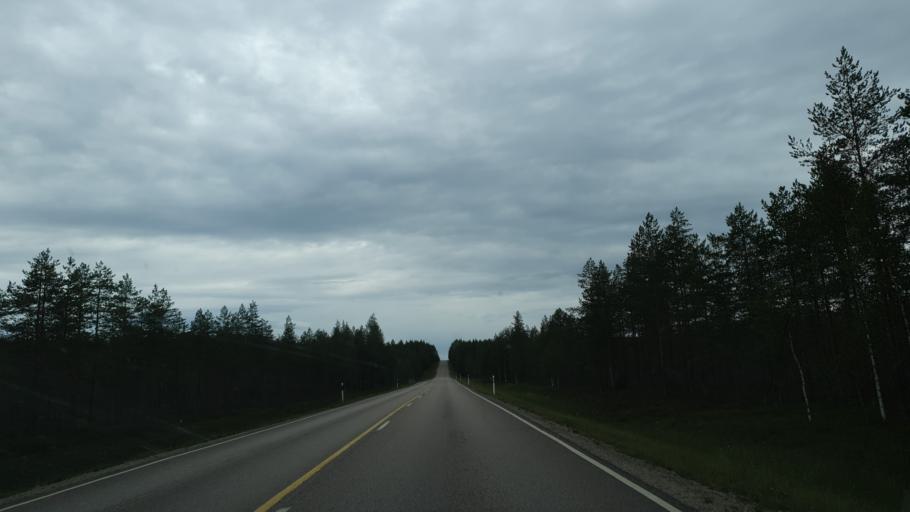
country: FI
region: Kainuu
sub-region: Kehys-Kainuu
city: Kuhmo
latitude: 64.4556
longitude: 29.4980
